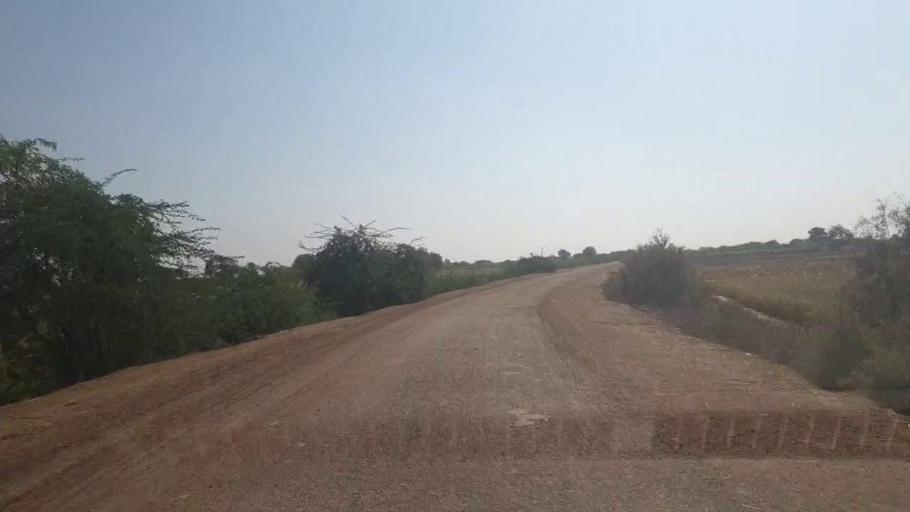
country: PK
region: Sindh
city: Badin
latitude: 24.5686
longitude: 68.8460
